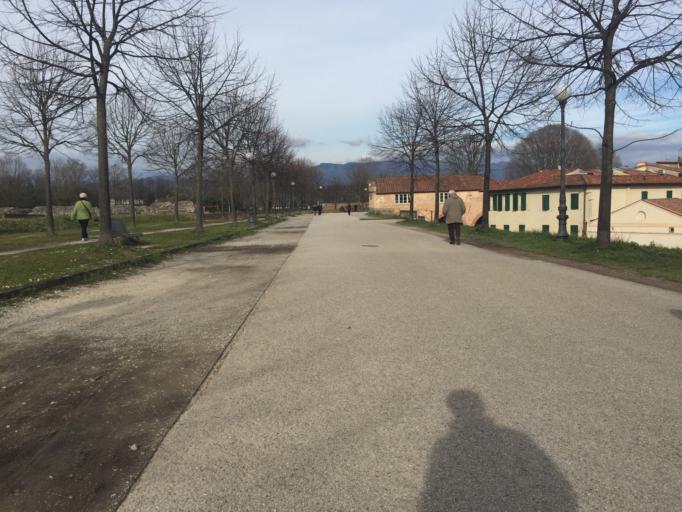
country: IT
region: Tuscany
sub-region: Provincia di Lucca
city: Lucca
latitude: 43.8451
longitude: 10.4970
